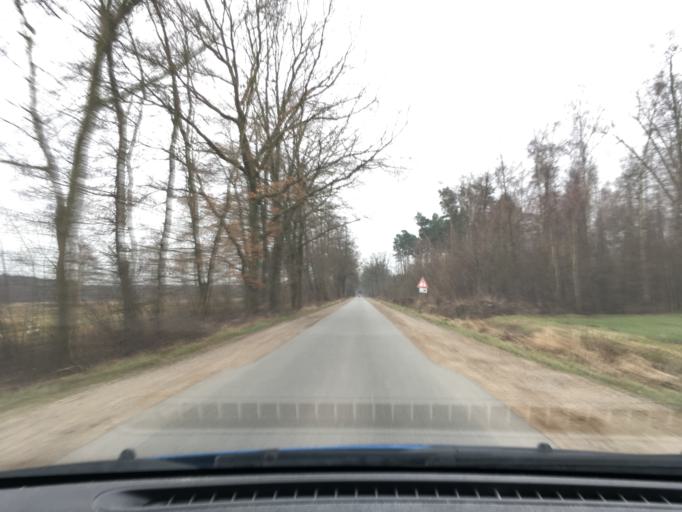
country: DE
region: Lower Saxony
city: Vogelsen
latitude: 53.2945
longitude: 10.3369
